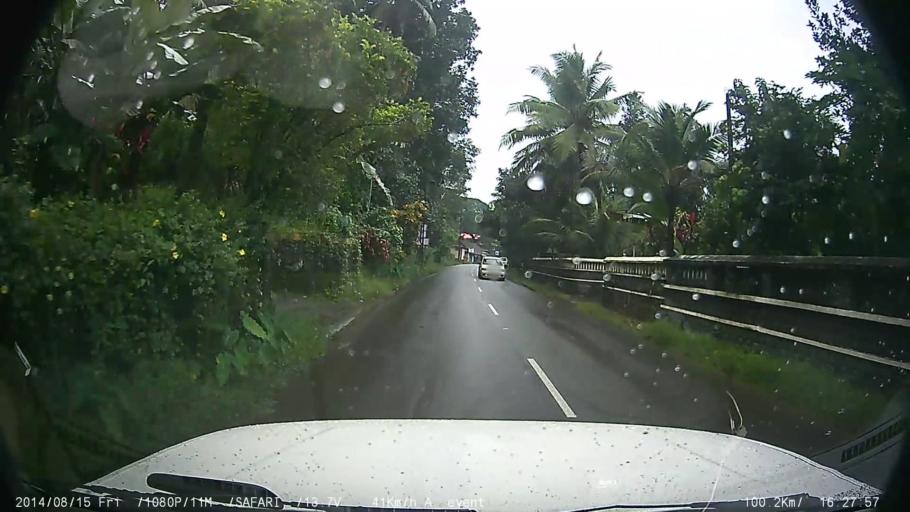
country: IN
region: Kerala
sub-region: Kottayam
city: Palackattumala
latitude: 9.7193
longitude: 76.6561
